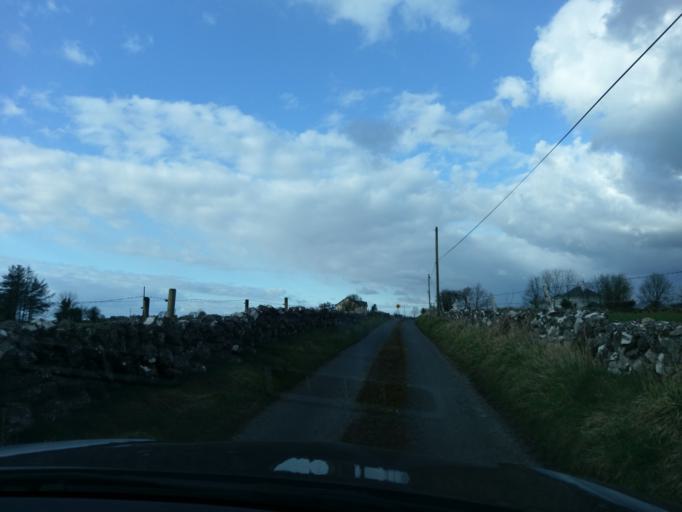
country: IE
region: Connaught
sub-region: County Galway
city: Athenry
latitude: 53.4534
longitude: -8.6431
